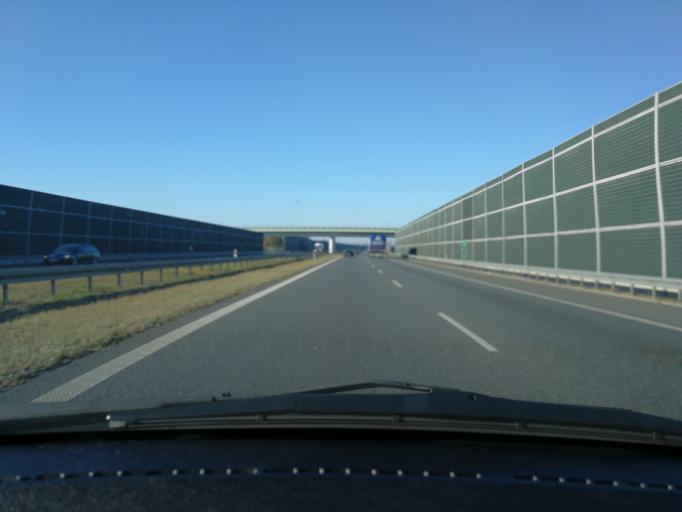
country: PL
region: Masovian Voivodeship
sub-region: Powiat zyrardowski
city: Guzow
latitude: 52.0768
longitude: 20.3275
